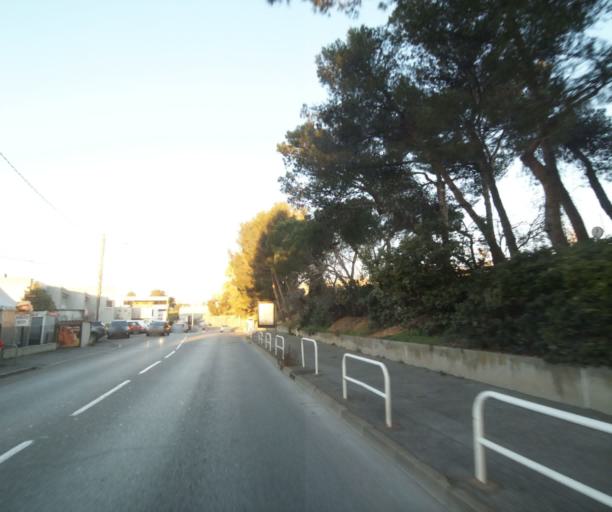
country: FR
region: Provence-Alpes-Cote d'Azur
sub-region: Departement des Alpes-Maritimes
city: Biot
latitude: 43.6026
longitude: 7.0901
